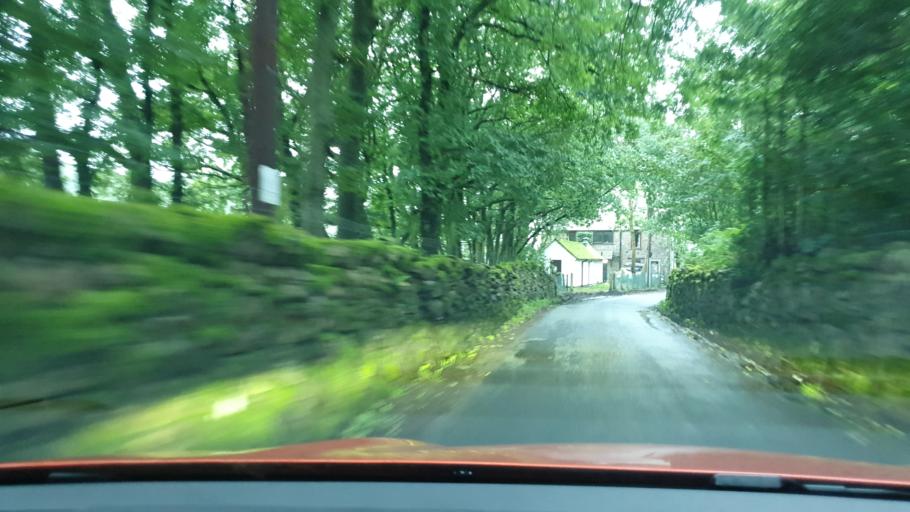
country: GB
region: England
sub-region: Cumbria
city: Seascale
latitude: 54.3897
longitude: -3.3032
